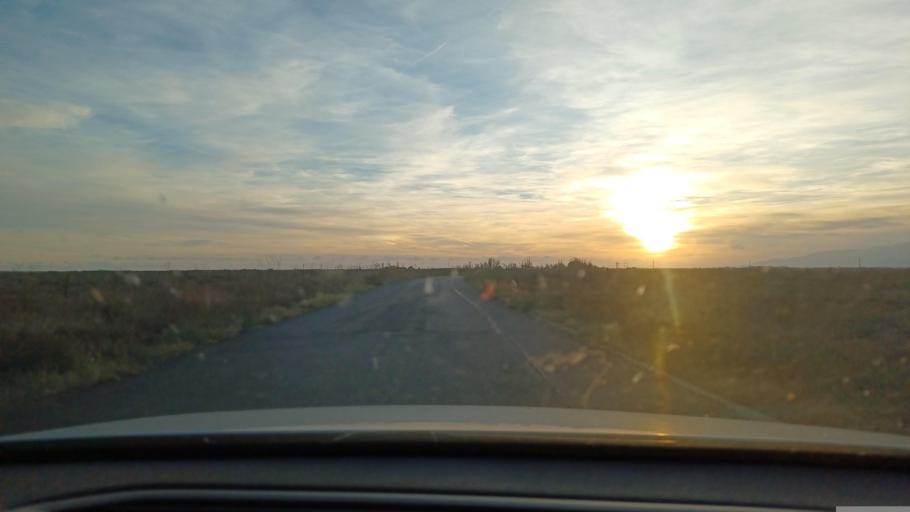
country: ES
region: Catalonia
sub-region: Provincia de Tarragona
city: Deltebre
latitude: 40.6547
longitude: 0.7703
